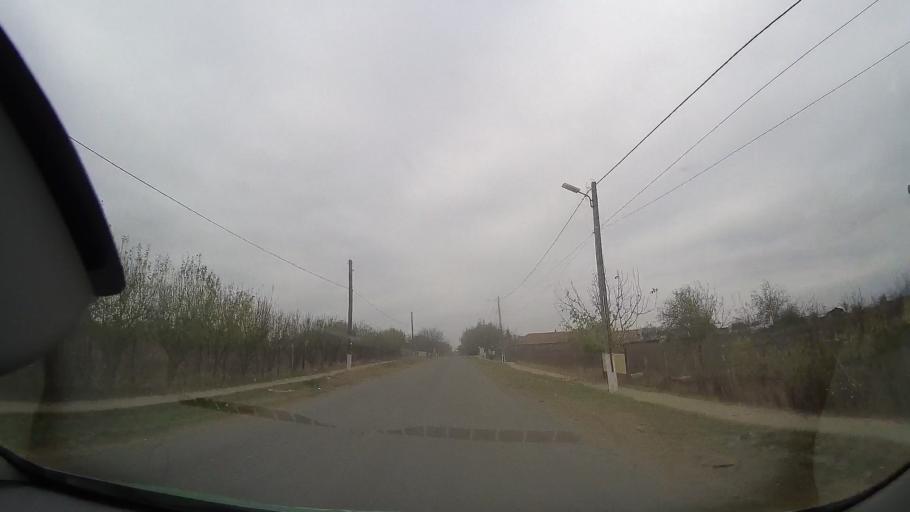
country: RO
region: Buzau
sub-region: Comuna Luciu
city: Luciu
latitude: 44.9734
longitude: 27.0732
